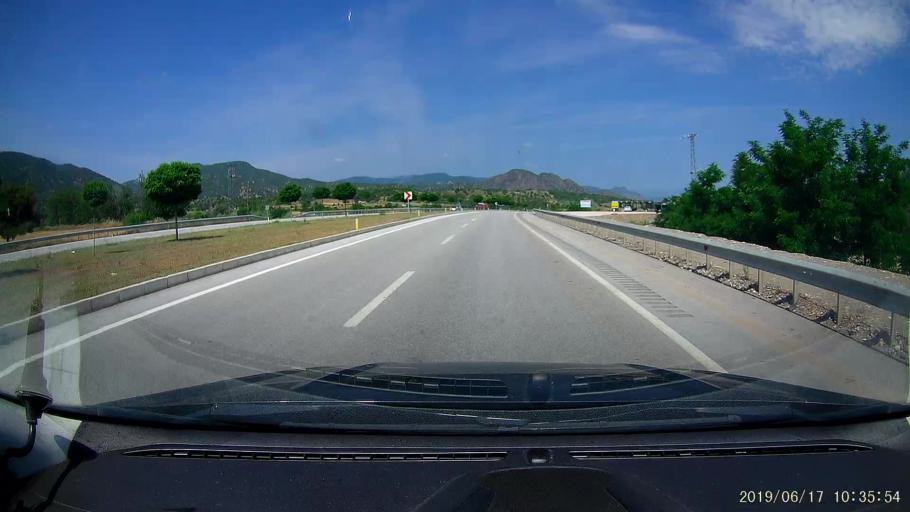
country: TR
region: Corum
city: Osmancik
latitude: 40.9724
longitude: 34.6923
